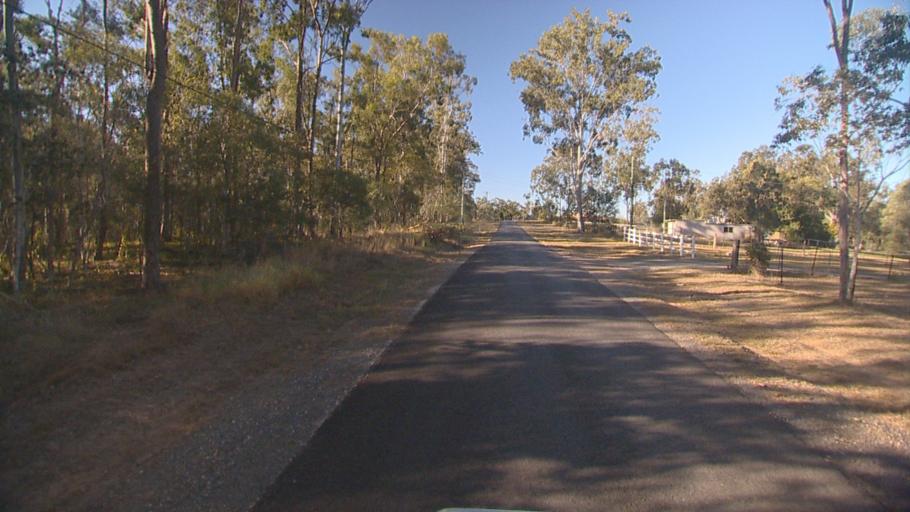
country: AU
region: Queensland
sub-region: Logan
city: North Maclean
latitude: -27.8116
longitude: 153.0480
